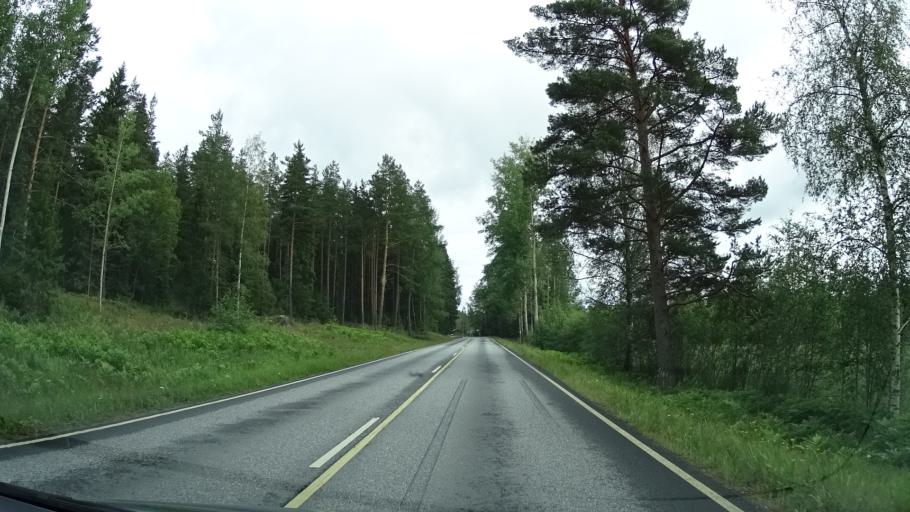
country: FI
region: Haeme
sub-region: Forssa
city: Humppila
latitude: 61.0941
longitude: 23.3684
